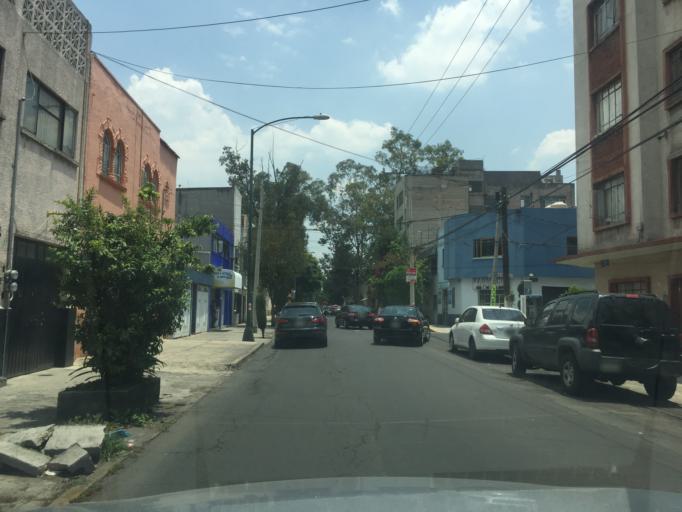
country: MX
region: Mexico
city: Colonia Lindavista
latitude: 19.4749
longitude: -99.1282
